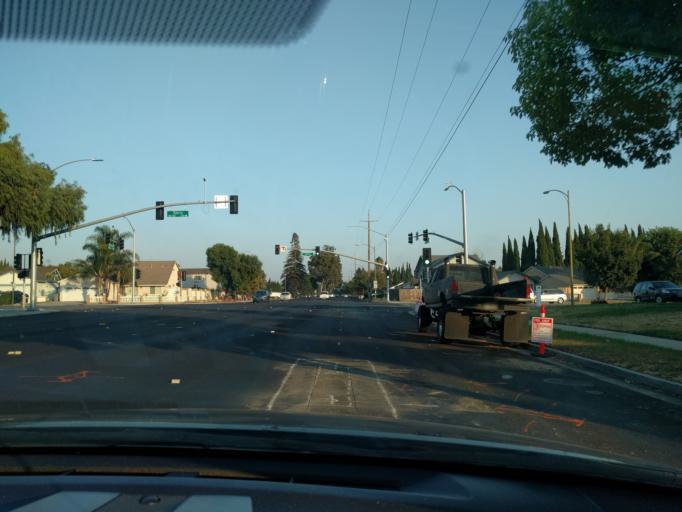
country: US
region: California
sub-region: Santa Clara County
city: Alum Rock
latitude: 37.3858
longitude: -121.8737
